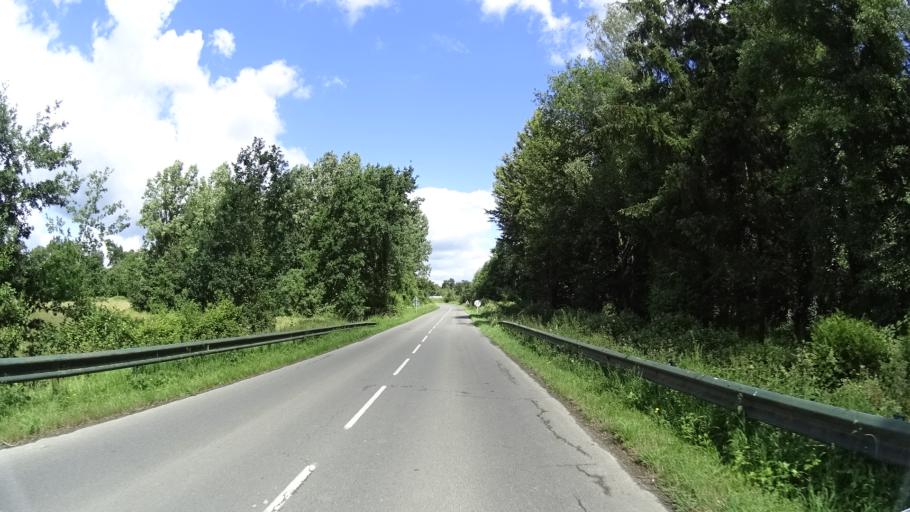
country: FR
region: Brittany
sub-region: Departement d'Ille-et-Vilaine
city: Saint-Gilles
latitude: 48.1353
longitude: -1.8253
